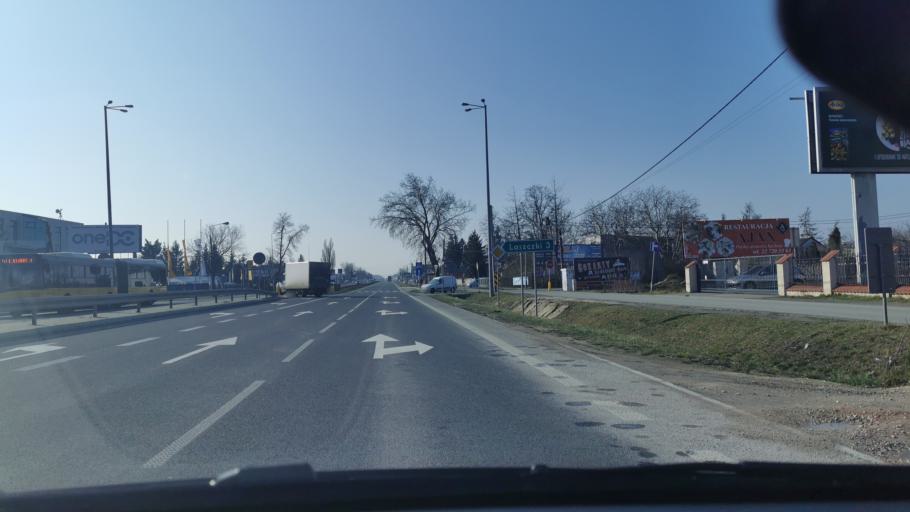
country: PL
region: Masovian Voivodeship
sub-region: Powiat pruszkowski
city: Nowe Grocholice
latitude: 52.1250
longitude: 20.8950
